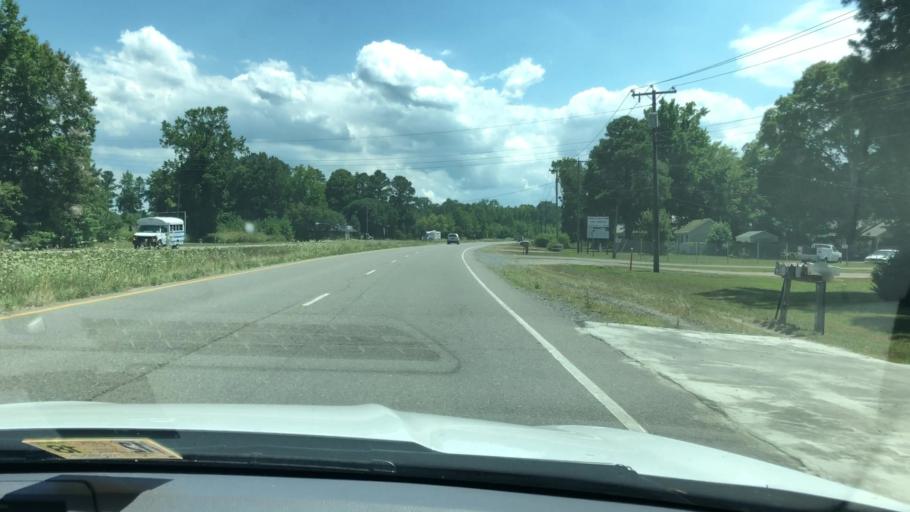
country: US
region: Virginia
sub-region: Middlesex County
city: Saluda
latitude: 37.5822
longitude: -76.6026
